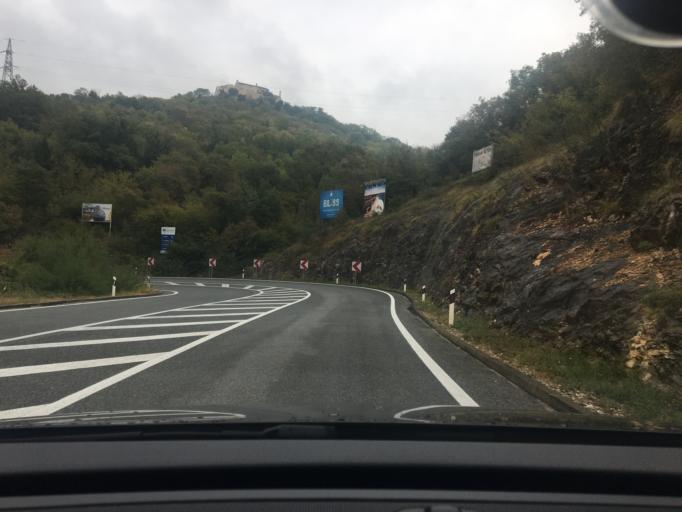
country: HR
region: Istarska
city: Buje
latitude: 45.4520
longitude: 13.6486
